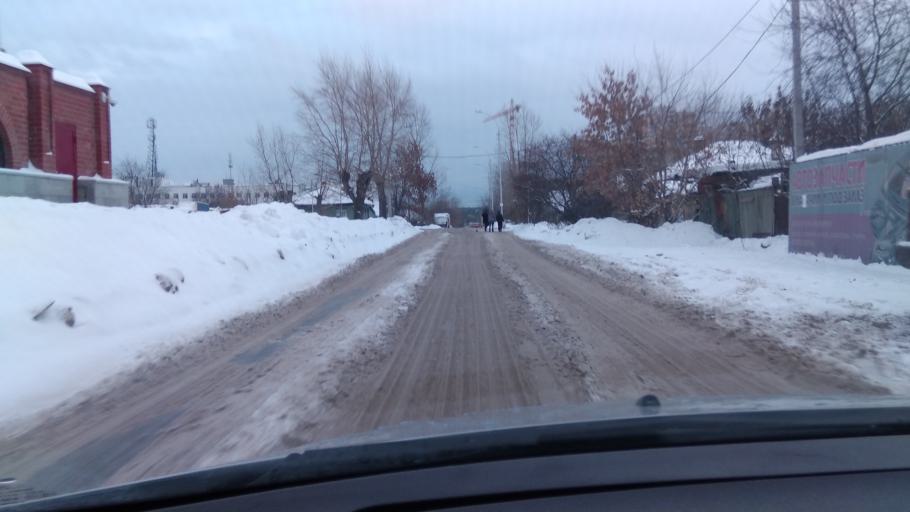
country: RU
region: Sverdlovsk
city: Yekaterinburg
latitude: 56.8049
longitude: 60.5966
